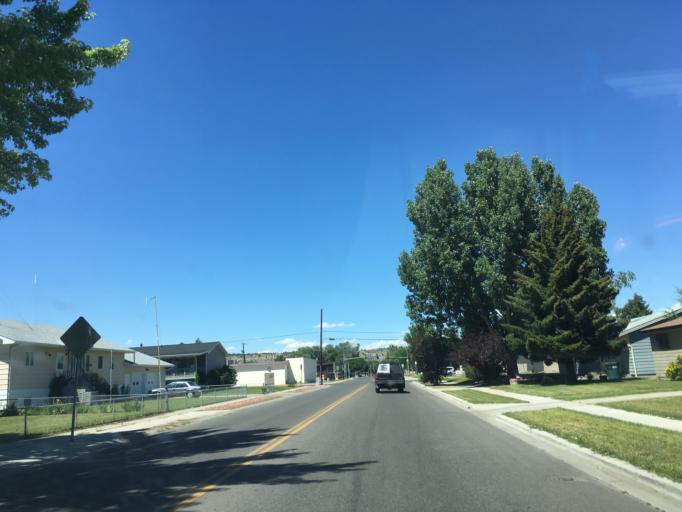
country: US
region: Montana
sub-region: Yellowstone County
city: Billings
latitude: 45.7752
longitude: -108.5642
